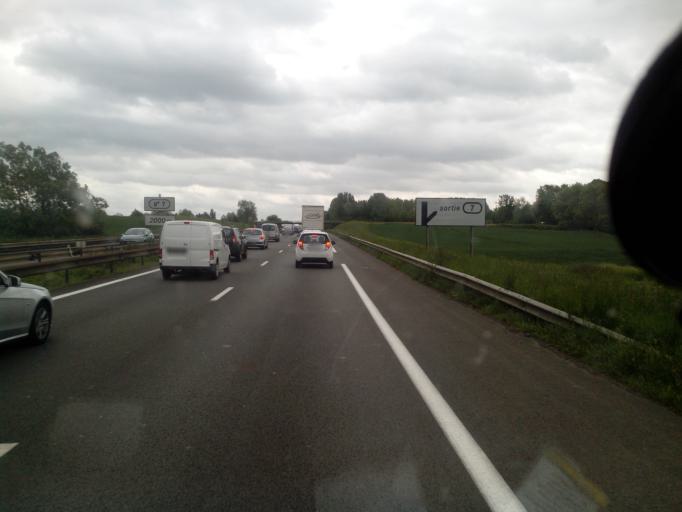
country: FR
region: Nord-Pas-de-Calais
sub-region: Departement du Nord
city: Ennetieres-en-Weppes
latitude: 50.6428
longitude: 2.9327
